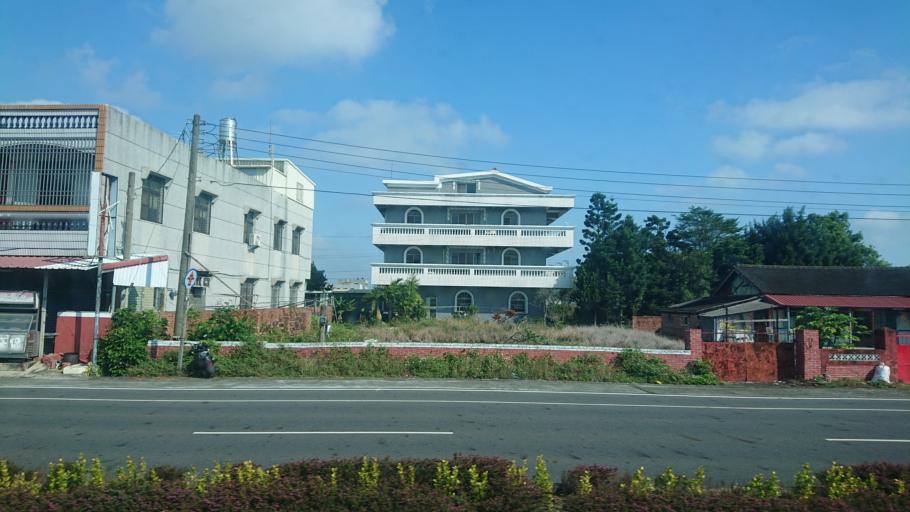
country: TW
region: Taiwan
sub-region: Chiayi
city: Taibao
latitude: 23.4586
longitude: 120.3036
